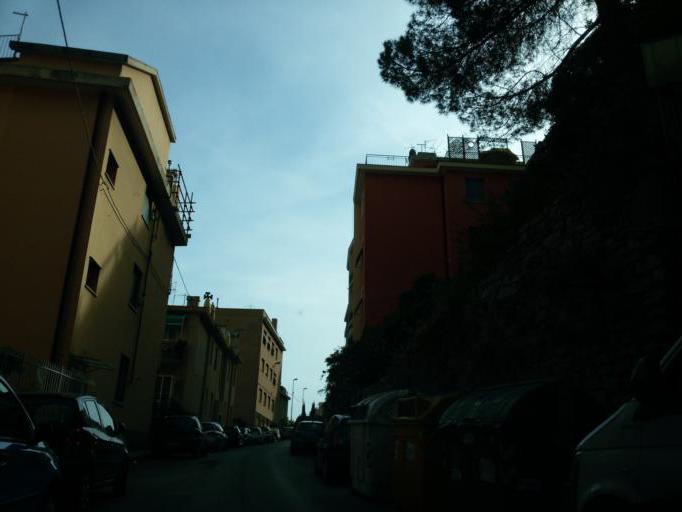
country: IT
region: Liguria
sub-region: Provincia di Genova
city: Genoa
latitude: 44.4215
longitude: 8.9574
